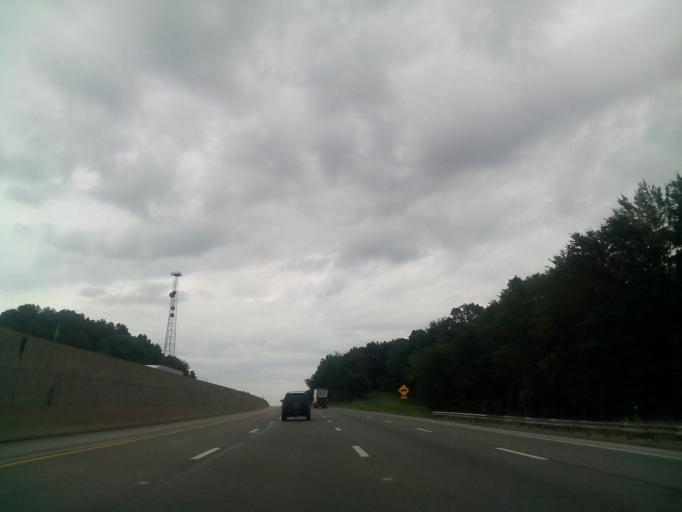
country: US
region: Ohio
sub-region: Erie County
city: Huron
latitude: 41.3288
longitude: -82.4841
